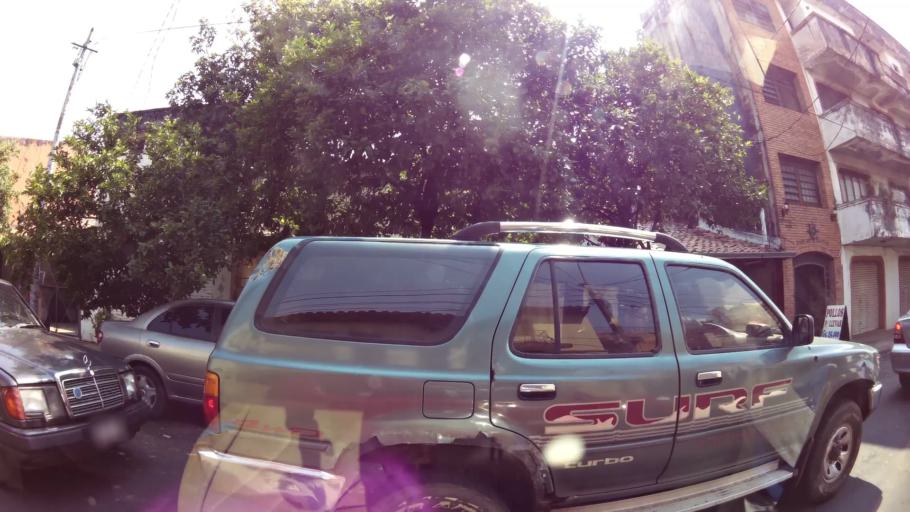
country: PY
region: Asuncion
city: Asuncion
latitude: -25.2886
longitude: -57.6470
